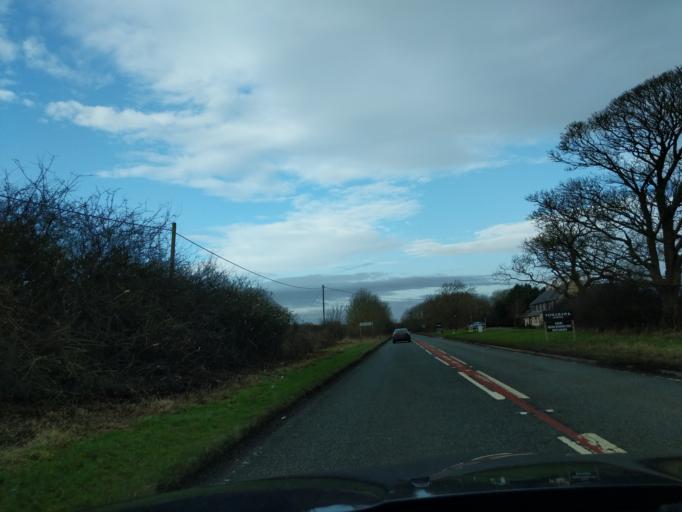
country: GB
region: England
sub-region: Northumberland
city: Darras Hall
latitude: 55.0754
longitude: -1.7981
